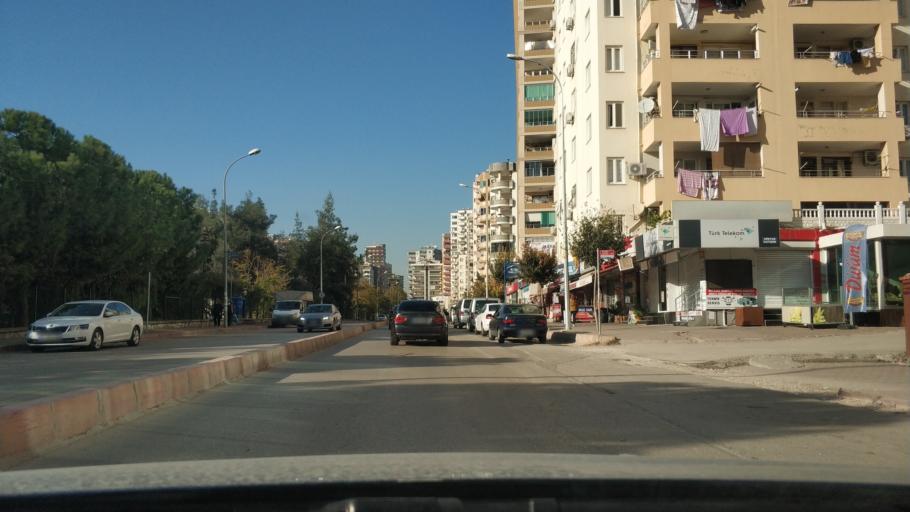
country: TR
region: Adana
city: Seyhan
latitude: 37.0495
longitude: 35.2801
